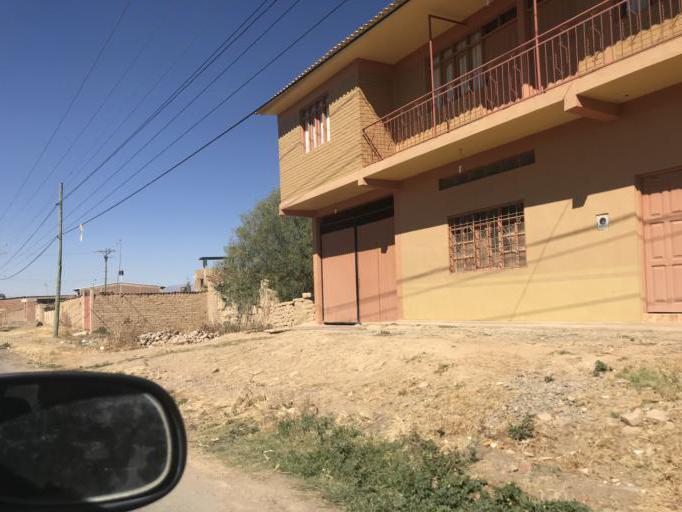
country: BO
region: Cochabamba
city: Tarata
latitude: -17.6026
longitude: -65.9830
